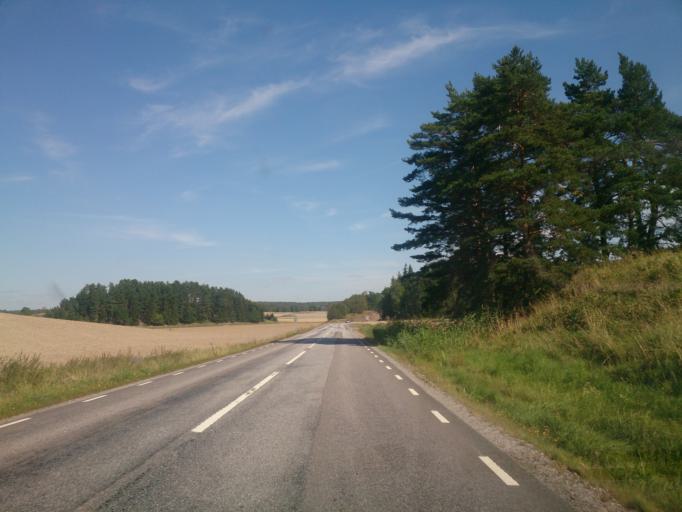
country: SE
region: OEstergoetland
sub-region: Norrkopings Kommun
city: Norrkoping
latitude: 58.4927
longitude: 16.1185
